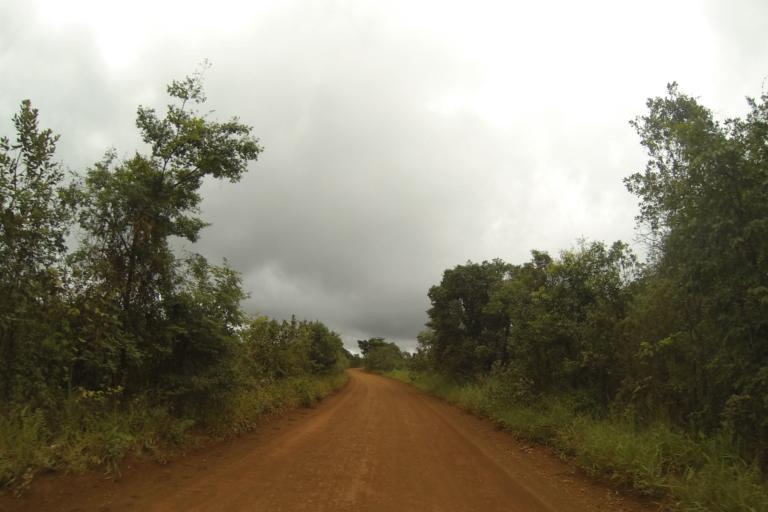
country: BR
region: Minas Gerais
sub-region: Campos Altos
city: Campos Altos
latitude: -19.8227
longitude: -46.3258
